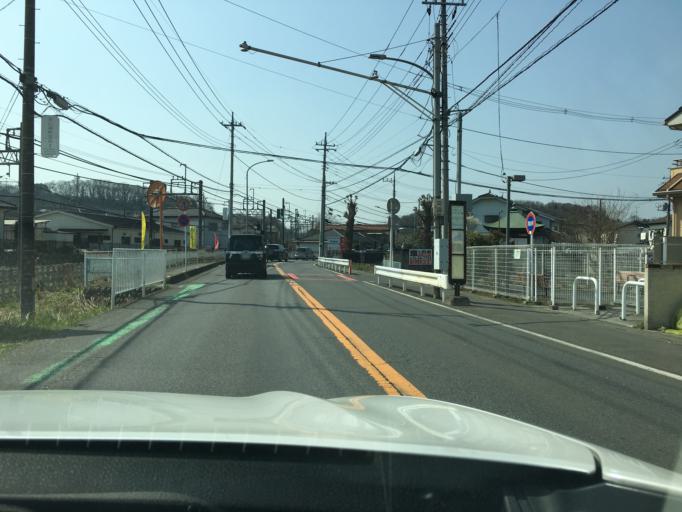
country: JP
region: Tokyo
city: Higashimurayama-shi
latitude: 35.7762
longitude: 139.4247
